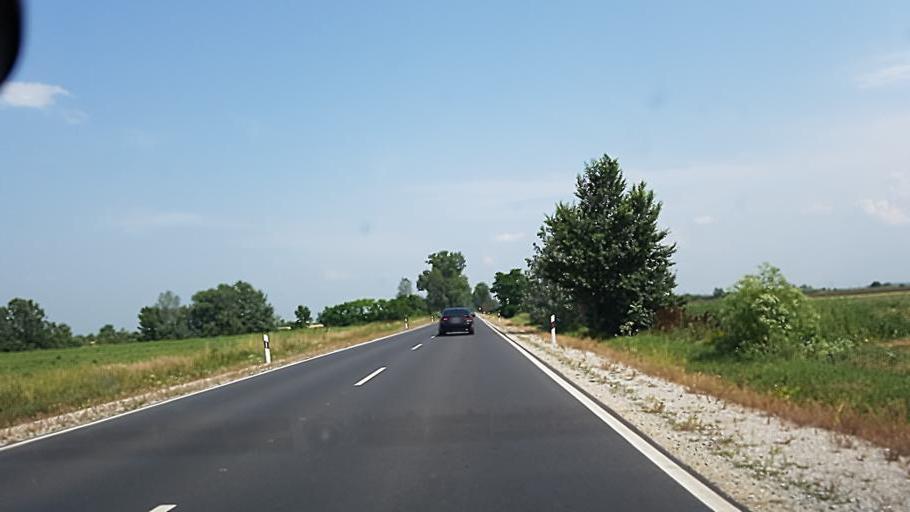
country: HU
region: Heves
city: Tiszanana
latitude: 47.6730
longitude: 20.5413
